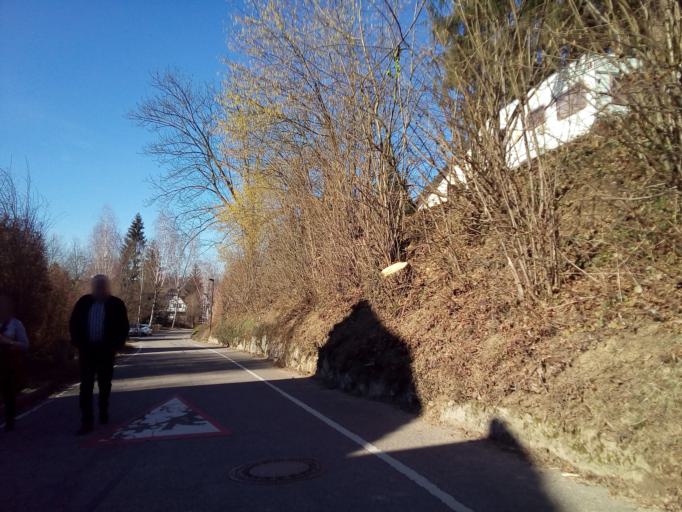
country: DE
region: Baden-Wuerttemberg
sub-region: Freiburg Region
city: Achern
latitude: 48.6168
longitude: 8.0596
